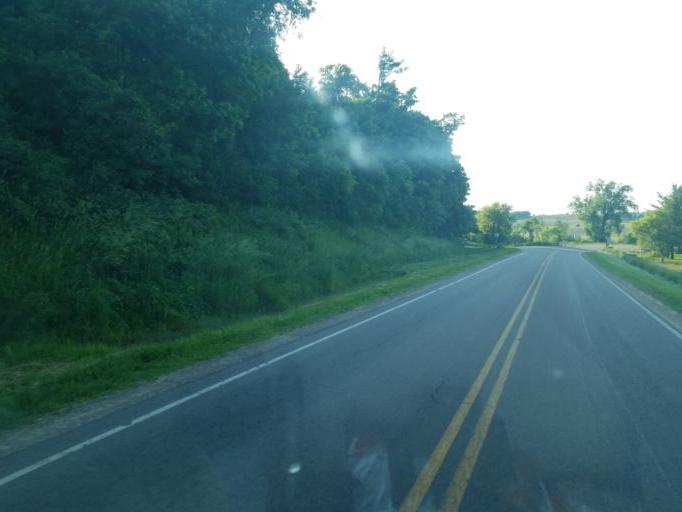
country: US
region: Wisconsin
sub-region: Vernon County
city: Hillsboro
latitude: 43.6333
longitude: -90.3519
